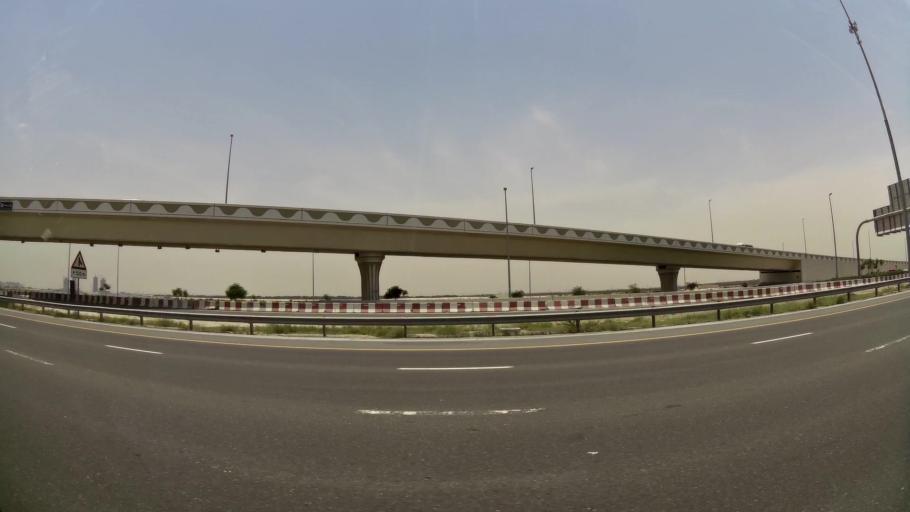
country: AE
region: Ash Shariqah
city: Sharjah
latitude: 25.2036
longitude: 55.3123
